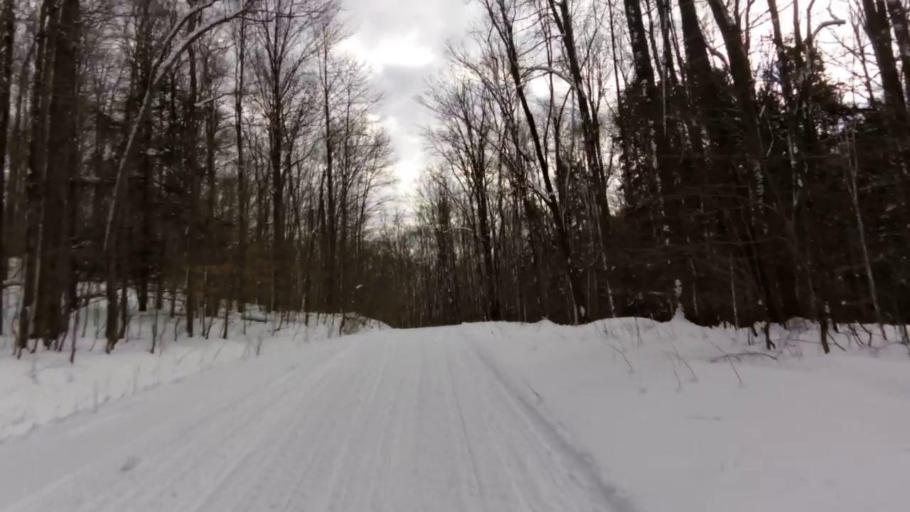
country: US
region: New York
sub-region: Cattaraugus County
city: Salamanca
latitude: 42.0517
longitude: -78.7529
